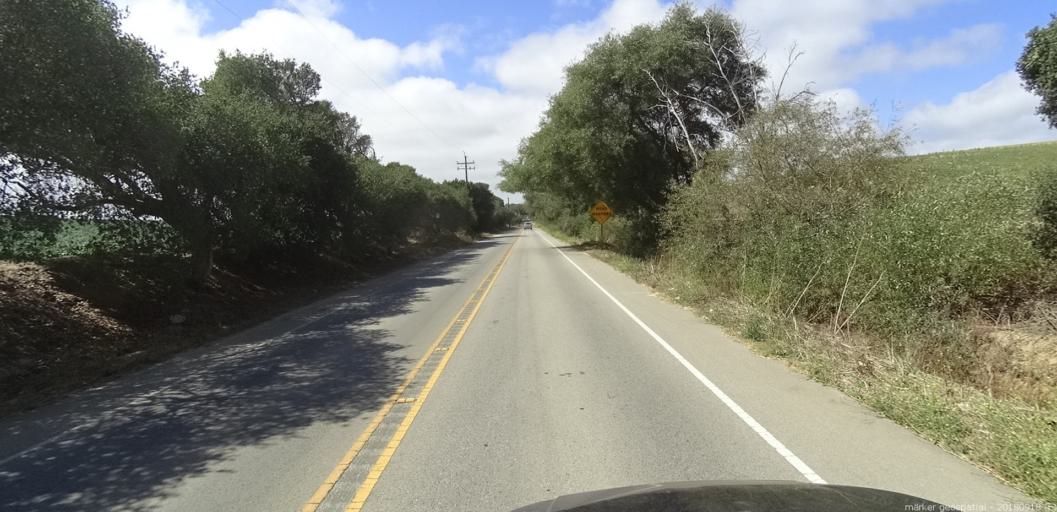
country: US
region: California
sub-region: Monterey County
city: Prunedale
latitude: 36.7765
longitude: -121.6953
